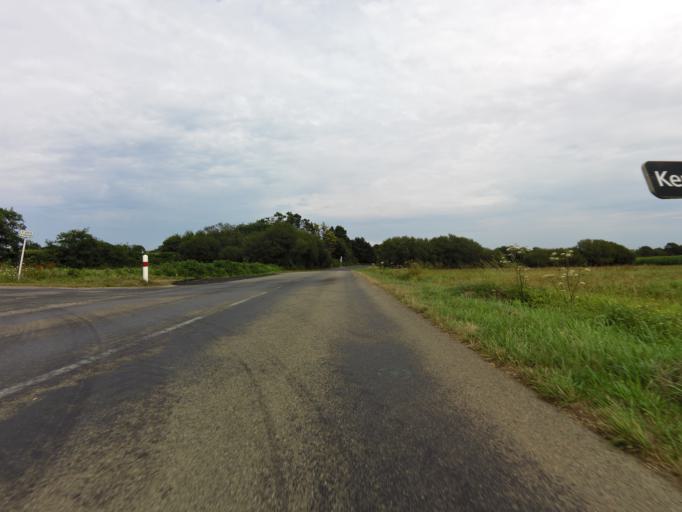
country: FR
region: Brittany
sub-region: Departement du Finistere
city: Poullan-sur-Mer
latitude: 48.0753
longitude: -4.4550
